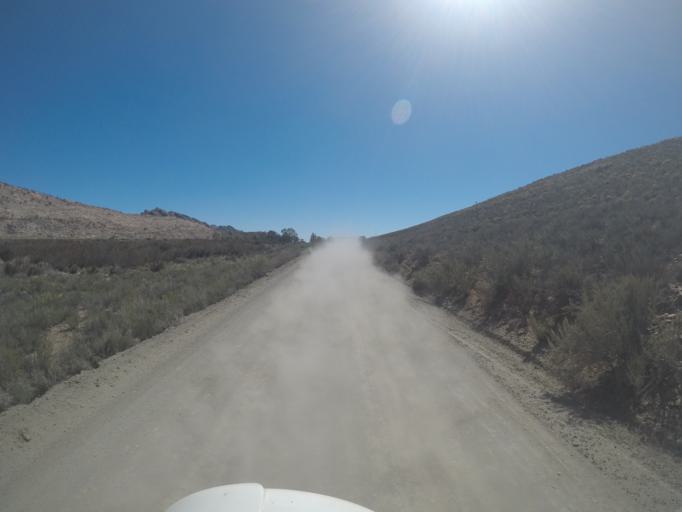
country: ZA
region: Western Cape
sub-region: Cape Winelands District Municipality
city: Ceres
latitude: -32.8184
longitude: 19.4522
